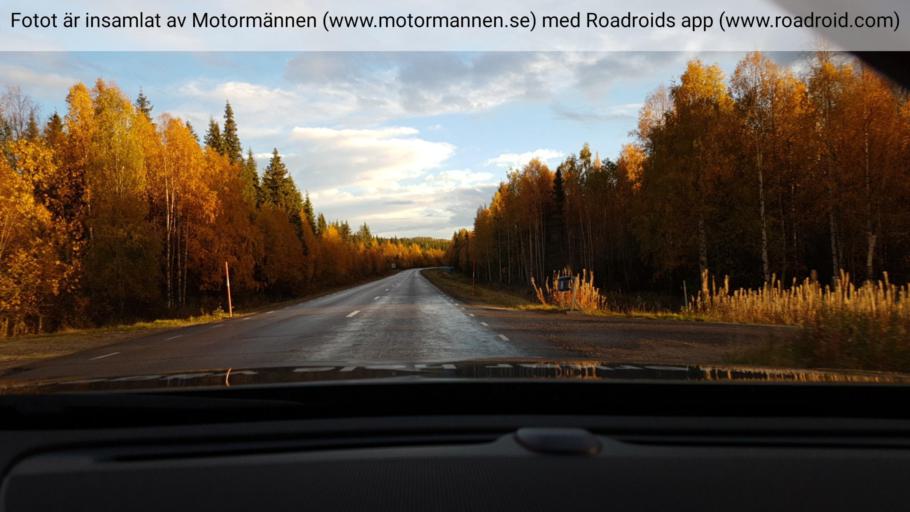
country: SE
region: Norrbotten
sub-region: Overkalix Kommun
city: OEverkalix
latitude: 66.6094
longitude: 22.7586
